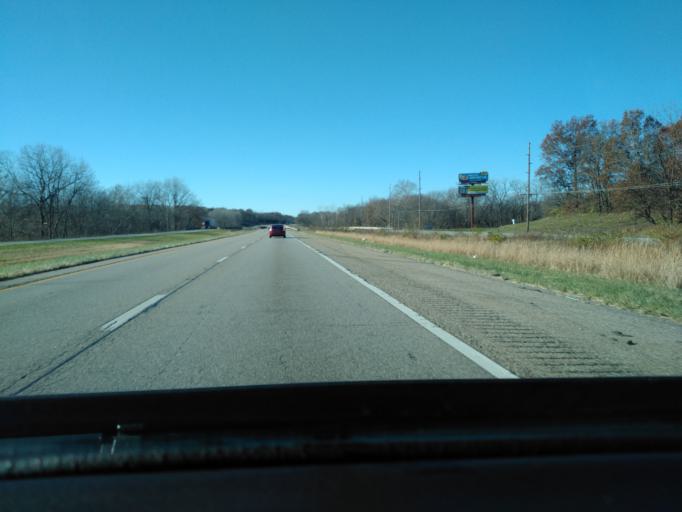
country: US
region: Illinois
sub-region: Bond County
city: Greenville
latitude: 38.8381
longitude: -89.5017
